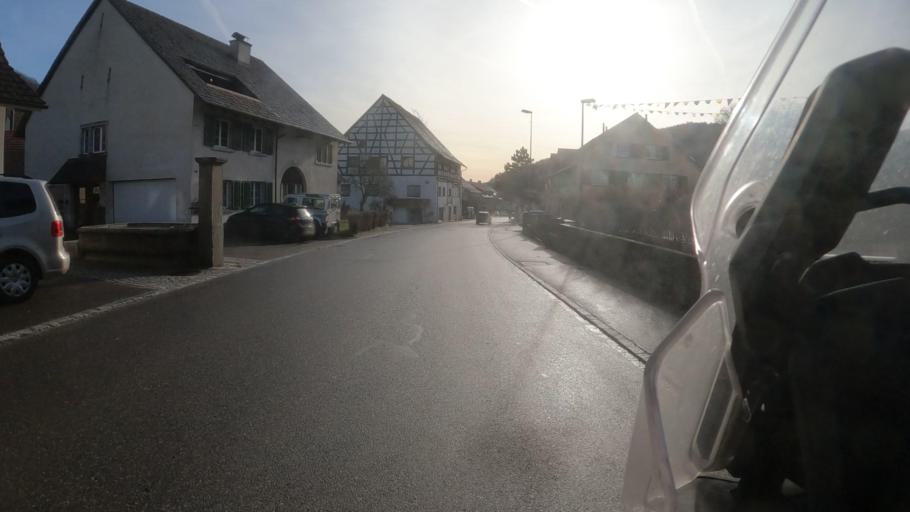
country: CH
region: Schaffhausen
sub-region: Bezirk Reiat
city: Stetten
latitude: 47.7605
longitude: 8.6096
